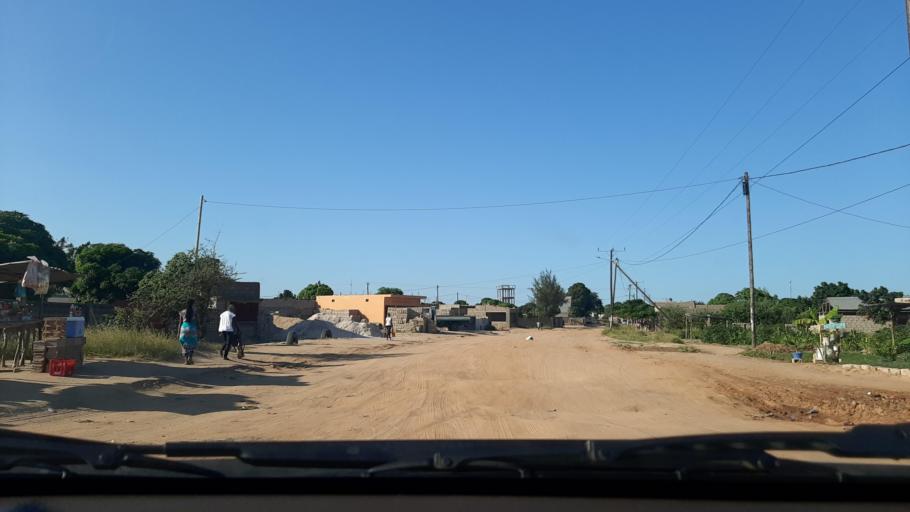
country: MZ
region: Maputo City
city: Maputo
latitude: -25.8031
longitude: 32.5474
